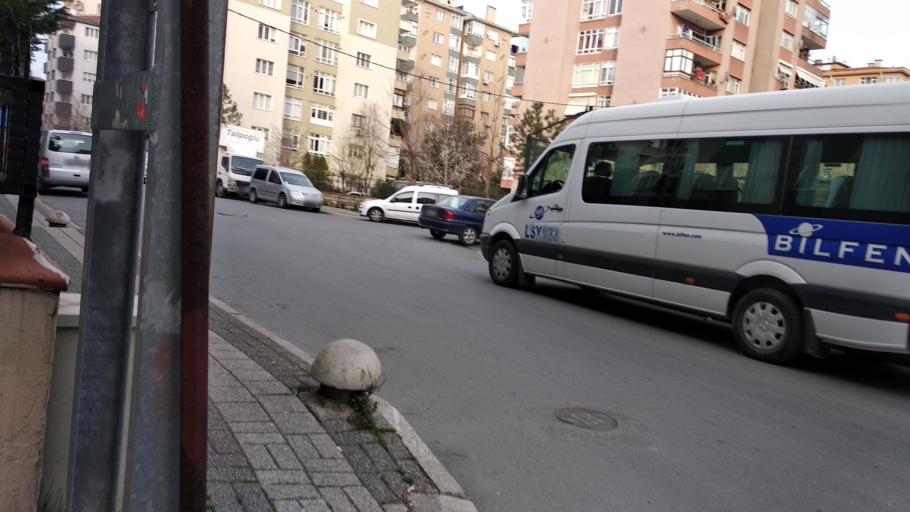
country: TR
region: Istanbul
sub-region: Atasehir
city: Atasehir
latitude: 40.9729
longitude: 29.1114
